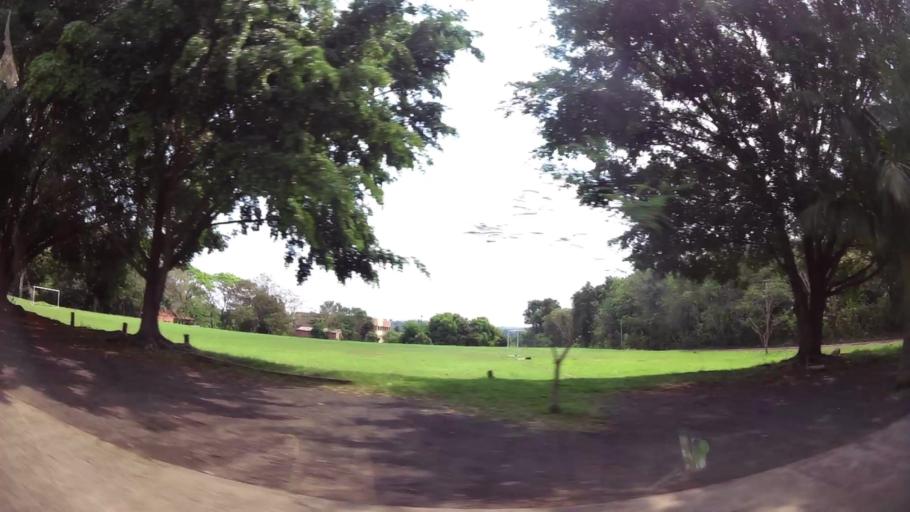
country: PY
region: Alto Parana
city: Ciudad del Este
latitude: -25.4751
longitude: -54.6219
